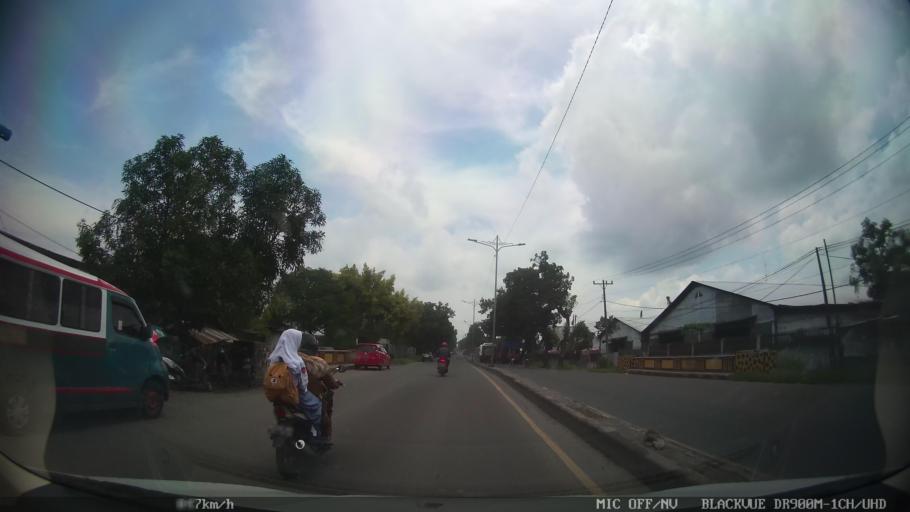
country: ID
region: North Sumatra
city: Labuhan Deli
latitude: 3.7029
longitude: 98.6778
